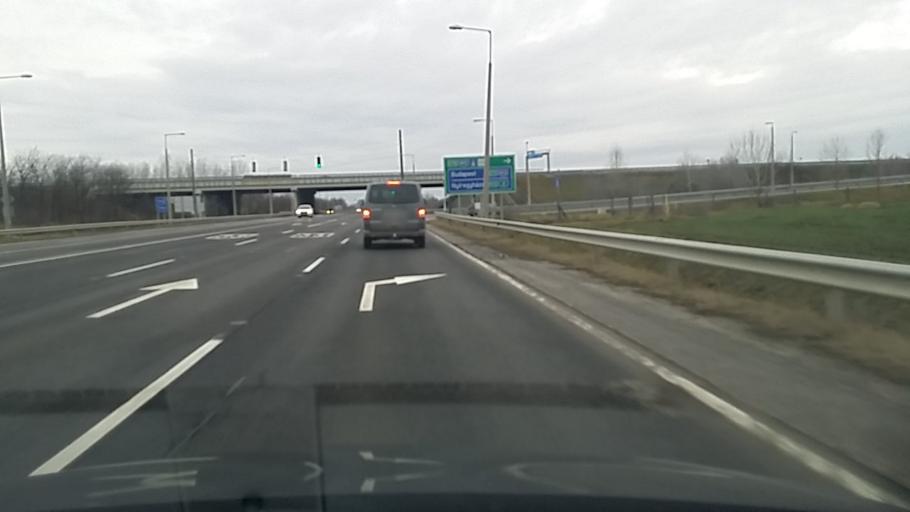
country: HU
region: Hajdu-Bihar
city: Debrecen
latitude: 47.5488
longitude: 21.5552
